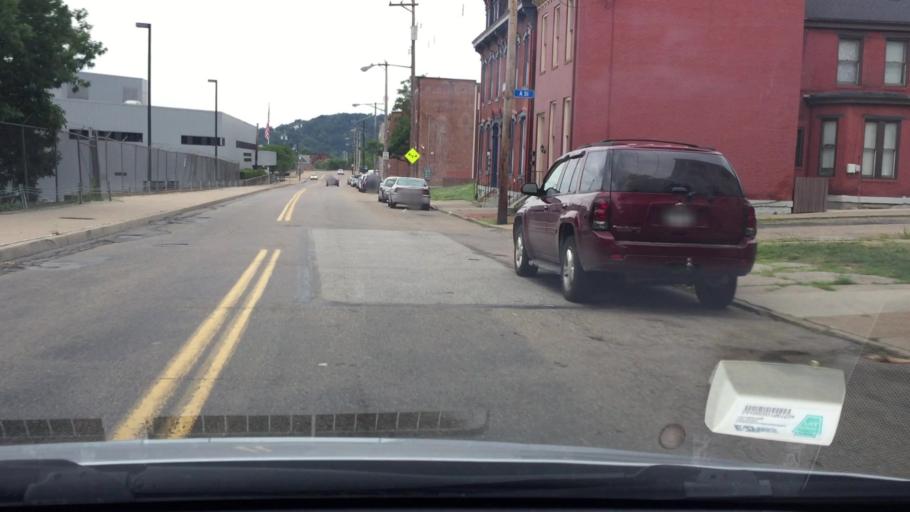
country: US
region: Pennsylvania
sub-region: Allegheny County
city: Pittsburgh
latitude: 40.4593
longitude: -80.0188
